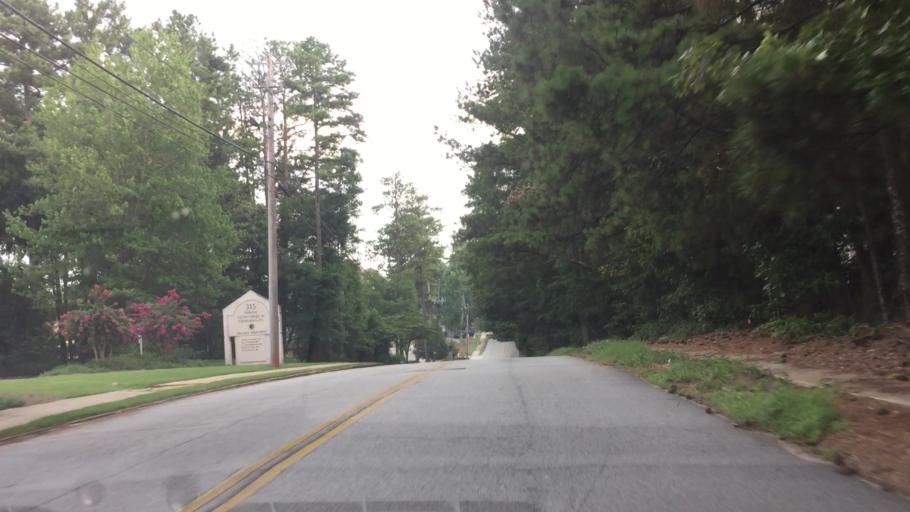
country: US
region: Georgia
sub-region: DeKalb County
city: Scottdale
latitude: 33.7846
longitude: -84.2794
